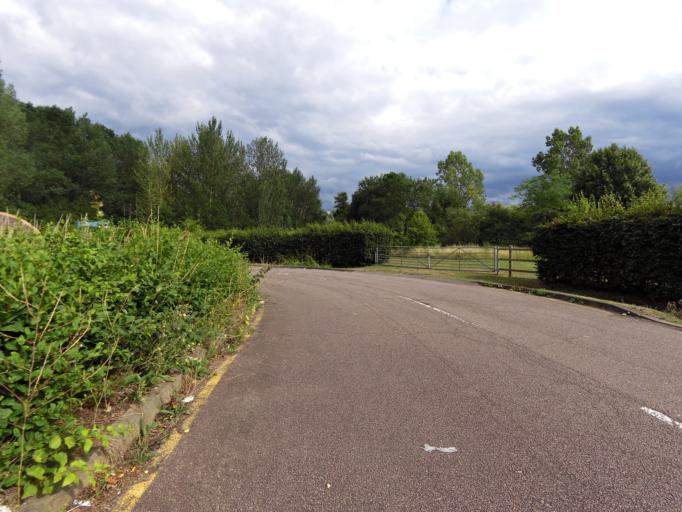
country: GB
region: England
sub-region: Hertfordshire
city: Broxbourne
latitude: 51.7434
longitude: -0.0089
